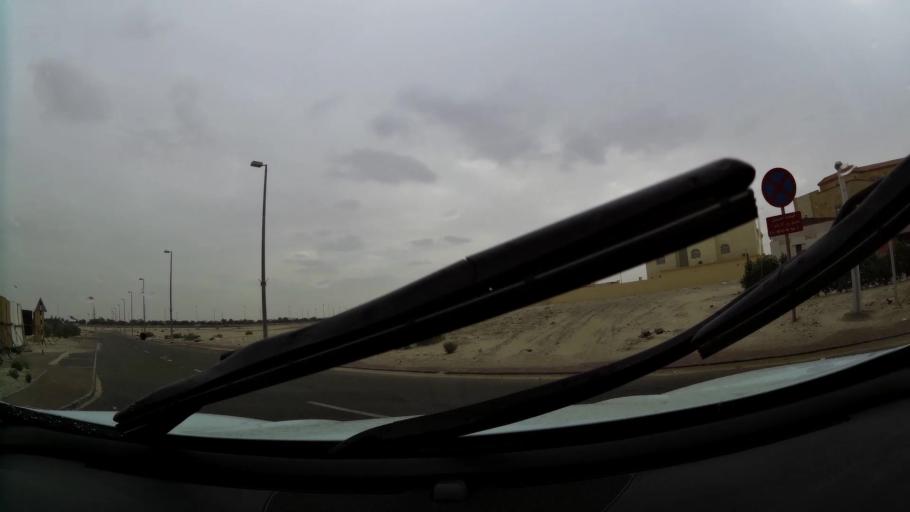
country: AE
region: Abu Dhabi
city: Abu Dhabi
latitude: 24.3658
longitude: 54.6455
